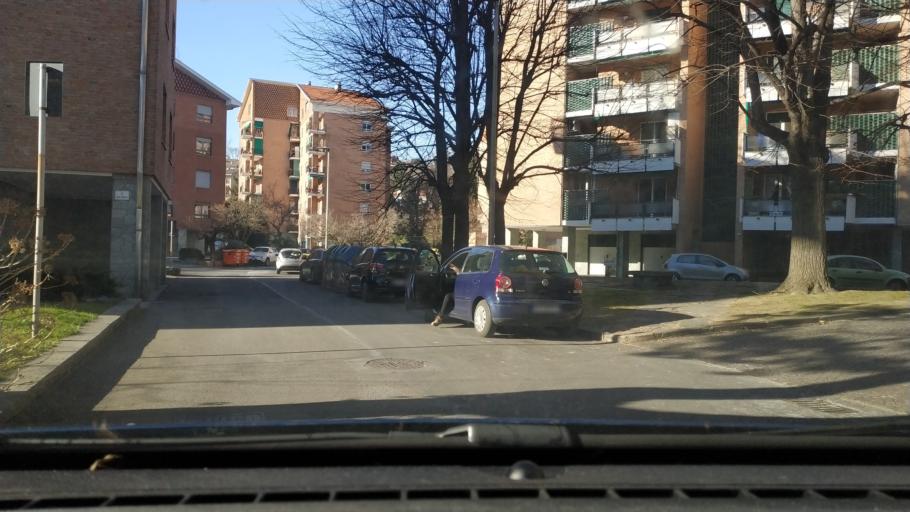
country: IT
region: Piedmont
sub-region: Provincia di Torino
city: Ivrea
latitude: 45.4706
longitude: 7.8873
